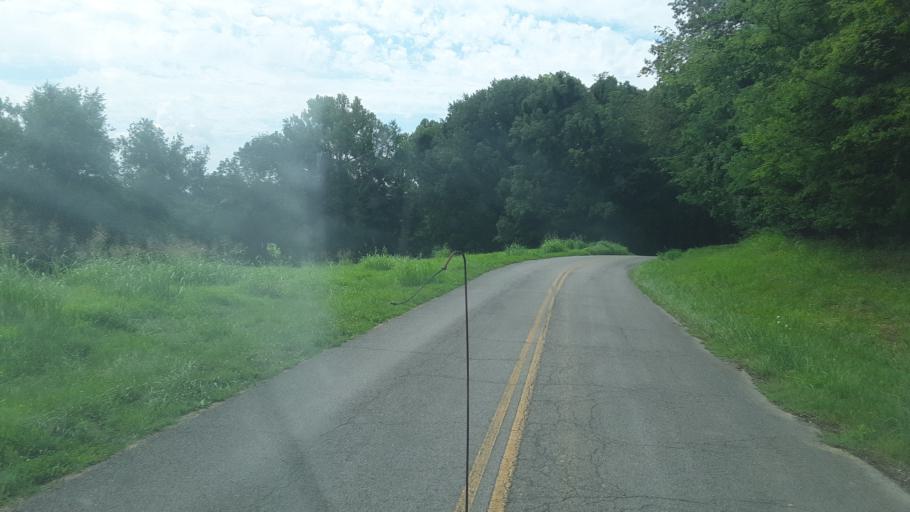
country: US
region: Kentucky
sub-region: Christian County
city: Oak Grove
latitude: 36.6441
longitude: -87.3437
